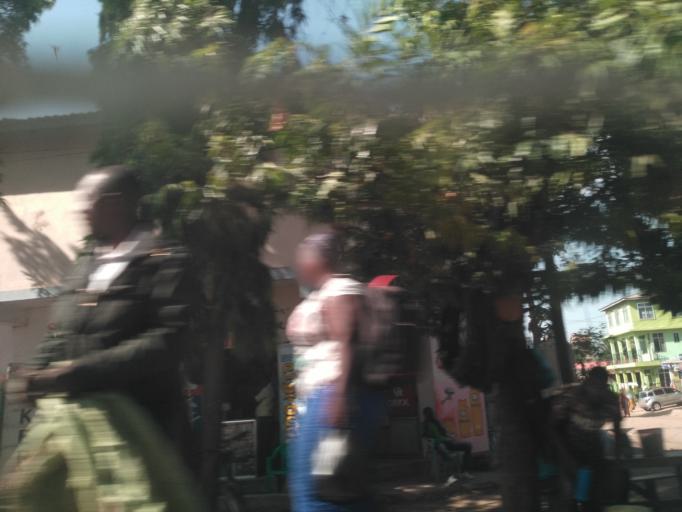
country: TZ
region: Mwanza
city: Mwanza
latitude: -2.5046
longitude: 32.9000
